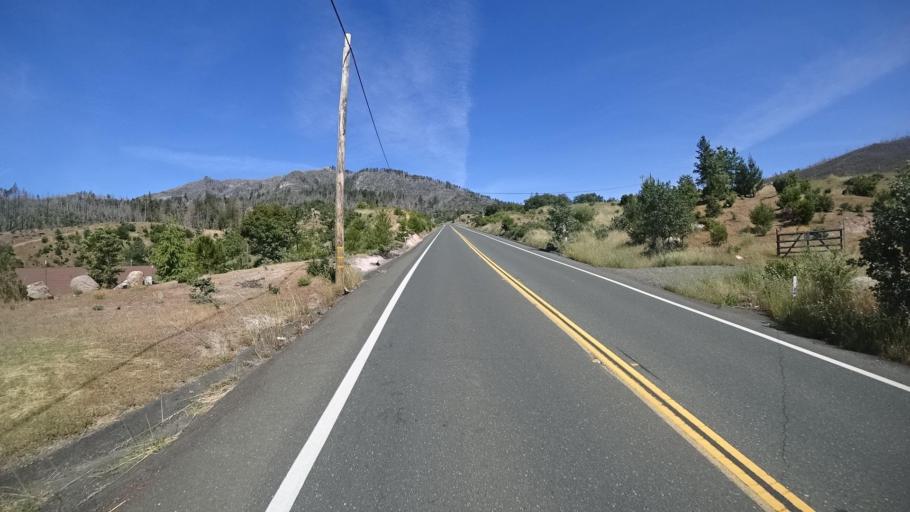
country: US
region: California
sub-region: Lake County
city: Cobb
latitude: 38.7921
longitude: -122.7014
